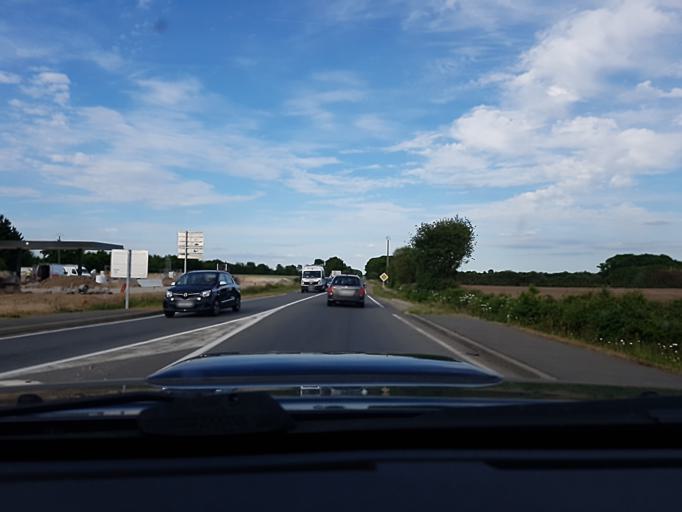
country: FR
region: Pays de la Loire
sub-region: Departement de la Vendee
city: Coex
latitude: 46.7056
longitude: -1.7222
